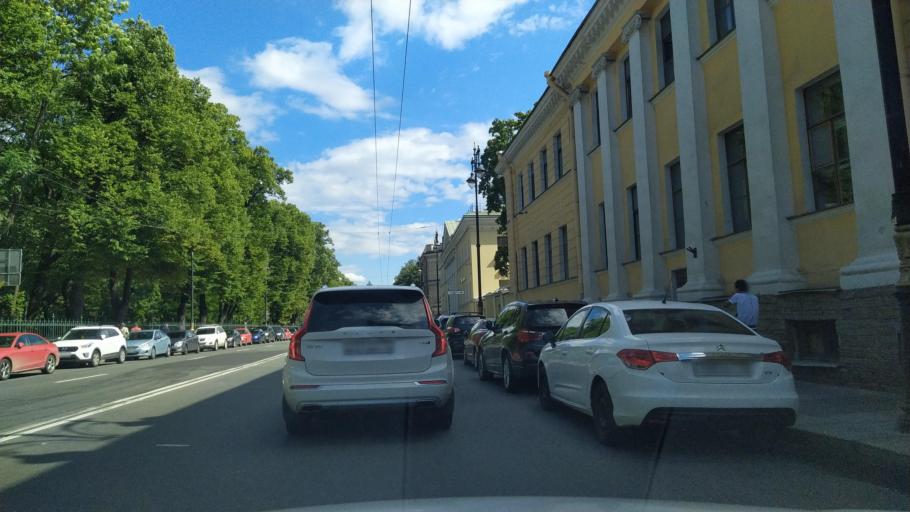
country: RU
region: St.-Petersburg
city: Centralniy
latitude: 59.9438
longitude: 30.3691
